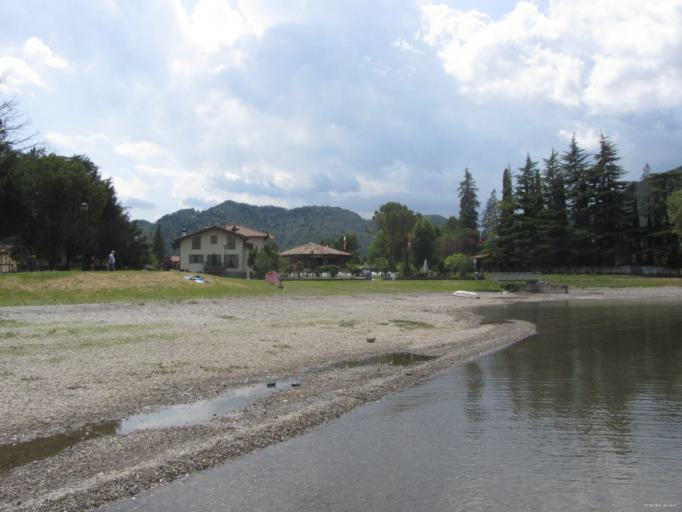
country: IT
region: Lombardy
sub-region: Provincia di Brescia
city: Crone
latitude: 45.7411
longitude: 10.4798
